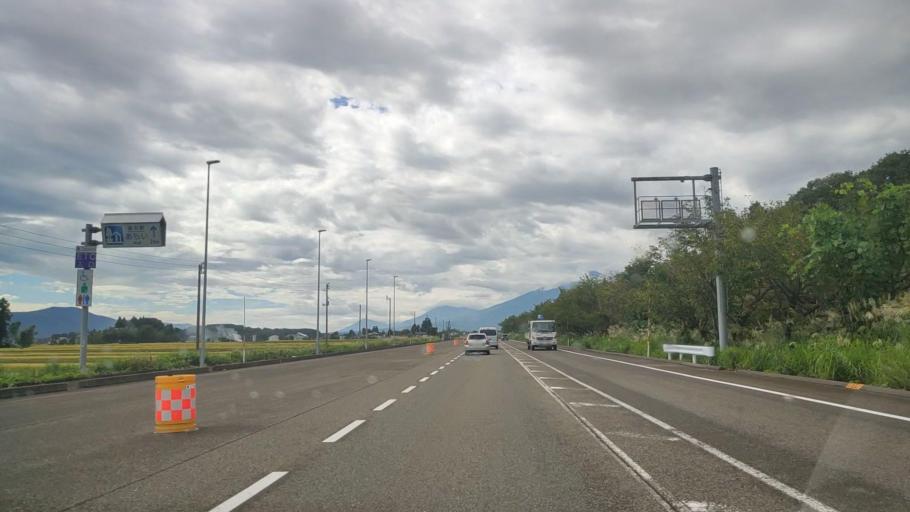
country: JP
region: Niigata
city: Arai
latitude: 37.0429
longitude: 138.2380
